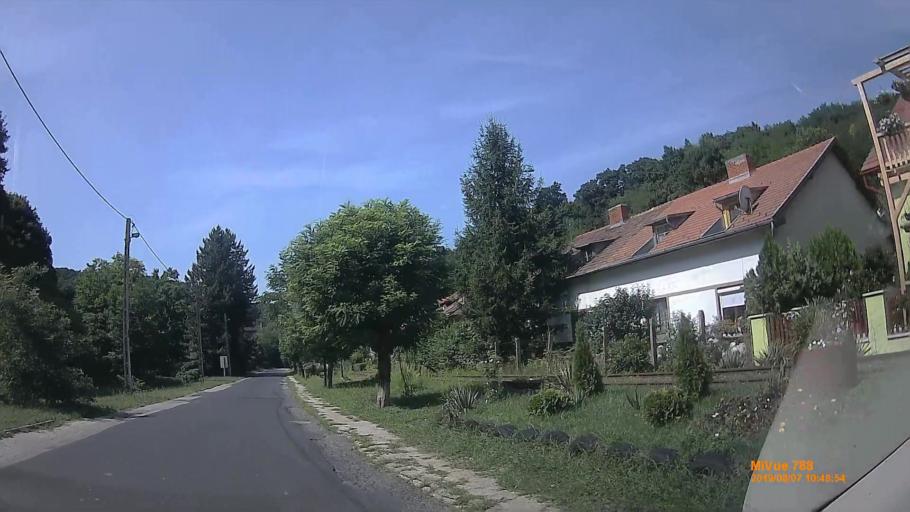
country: HU
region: Veszprem
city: Ajka
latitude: 47.0872
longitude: 17.5817
